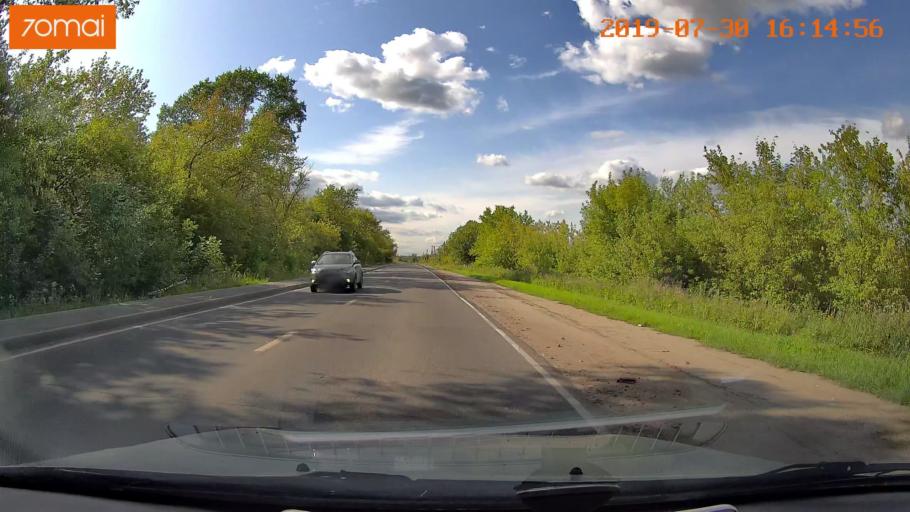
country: RU
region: Moskovskaya
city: Voskresensk
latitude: 55.2926
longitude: 38.6730
